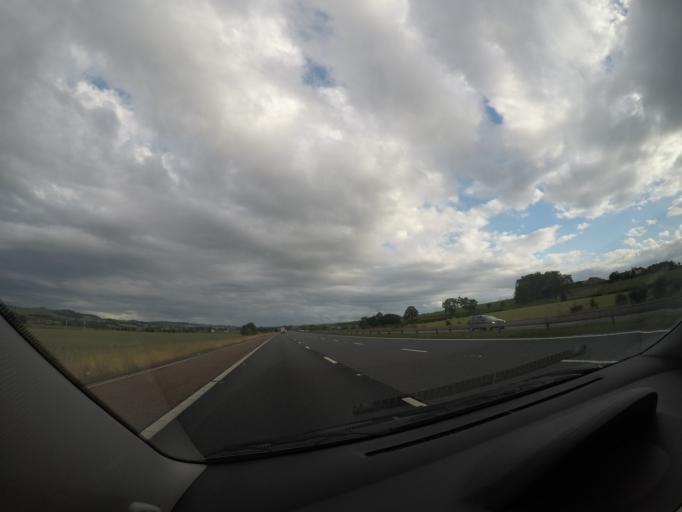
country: GB
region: England
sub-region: Cumbria
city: Penrith
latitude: 54.7318
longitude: -2.8032
